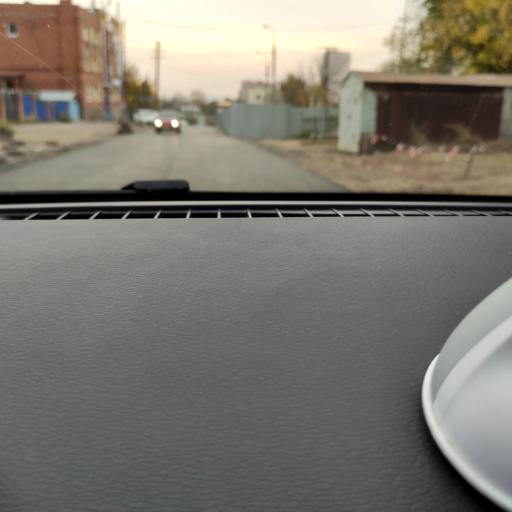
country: RU
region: Samara
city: Samara
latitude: 53.1931
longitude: 50.2113
